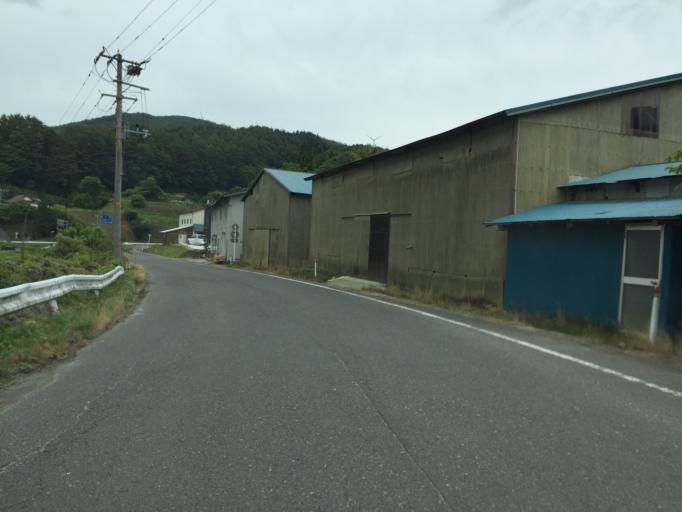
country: JP
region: Fukushima
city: Funehikimachi-funehiki
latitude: 37.3972
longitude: 140.6919
